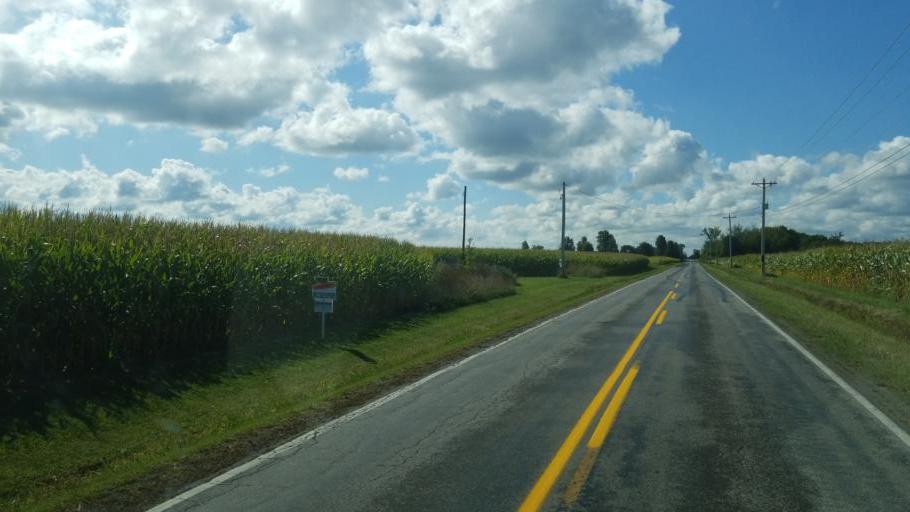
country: US
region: Ohio
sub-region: Lorain County
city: Oberlin
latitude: 41.2571
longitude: -82.1798
